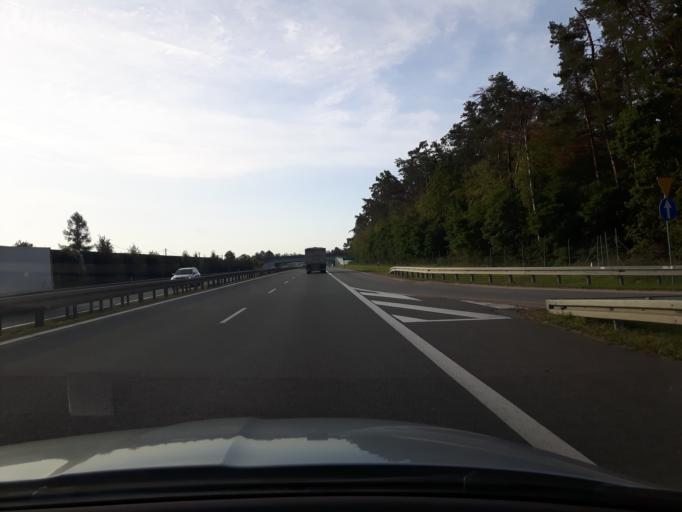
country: PL
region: Masovian Voivodeship
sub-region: Powiat bialobrzeski
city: Sucha
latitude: 51.6200
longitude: 20.9748
